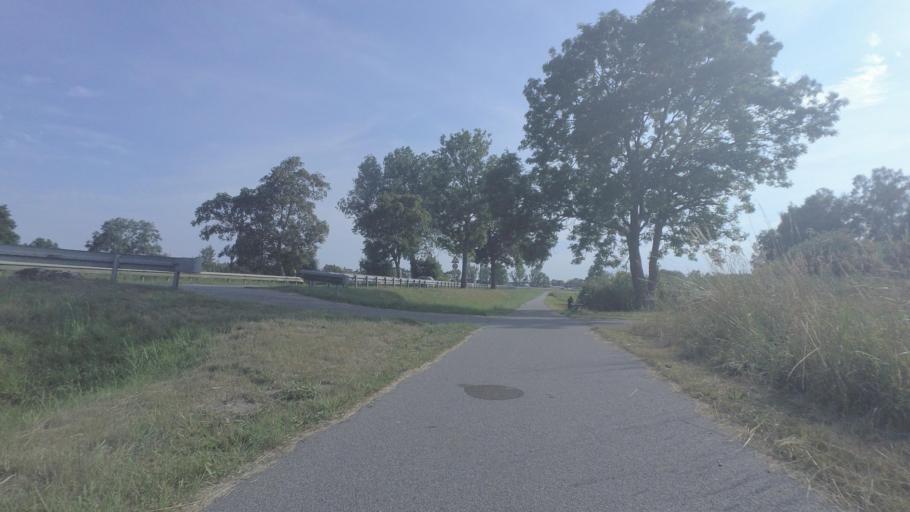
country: DE
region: Mecklenburg-Vorpommern
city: Tutow
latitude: 53.9820
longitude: 13.1495
